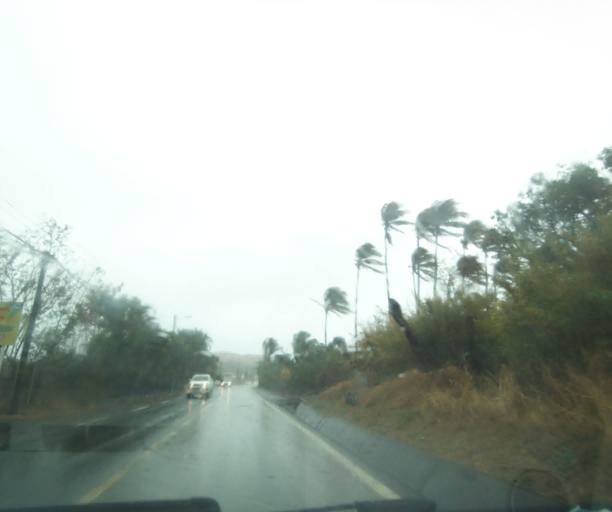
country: RE
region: Reunion
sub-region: Reunion
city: Saint-Paul
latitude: -21.0465
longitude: 55.2378
